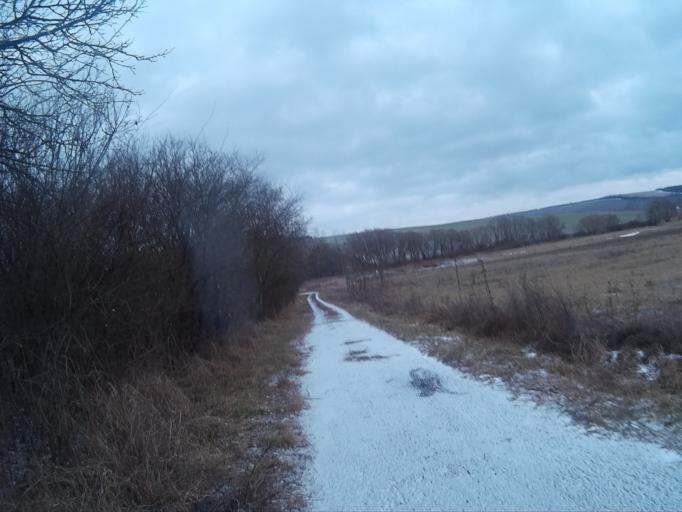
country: HU
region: Borsod-Abauj-Zemplen
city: Halmaj
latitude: 48.3671
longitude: 20.9505
